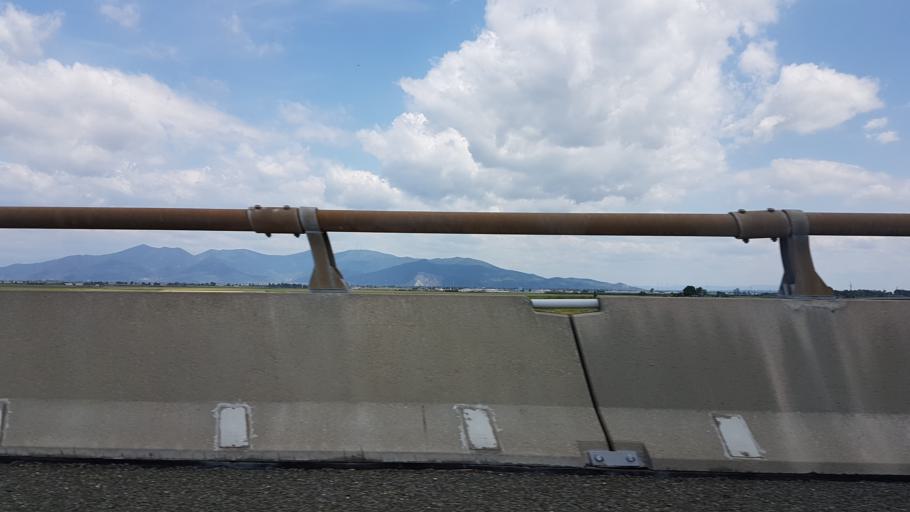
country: IT
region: Tuscany
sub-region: Provincia di Livorno
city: Vicarello
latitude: 43.6165
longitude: 10.4358
